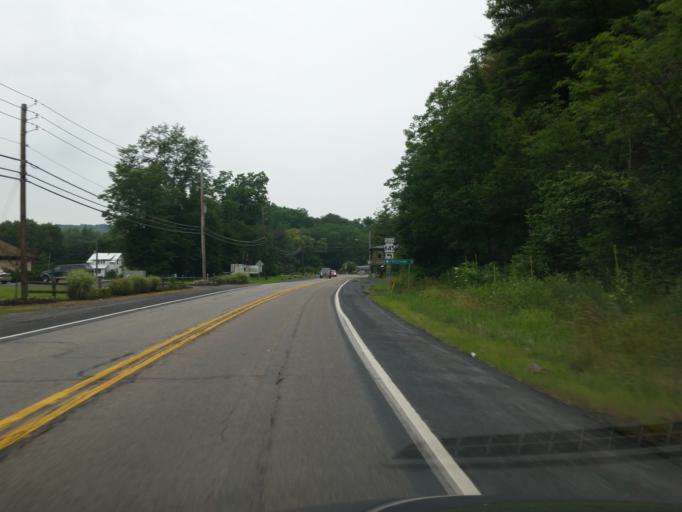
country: US
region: Pennsylvania
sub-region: Schuylkill County
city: Pine Grove
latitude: 40.5400
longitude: -76.3882
